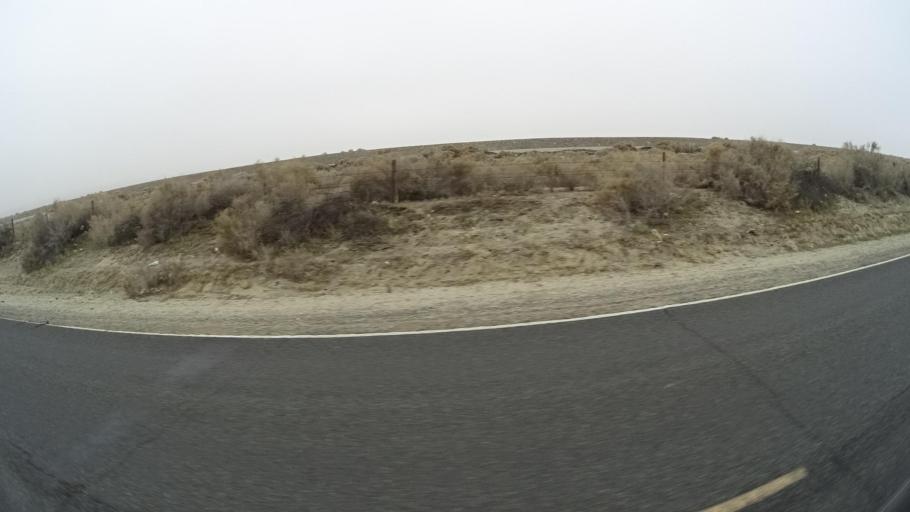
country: US
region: California
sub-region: Kern County
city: Buttonwillow
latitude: 35.3519
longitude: -119.4718
